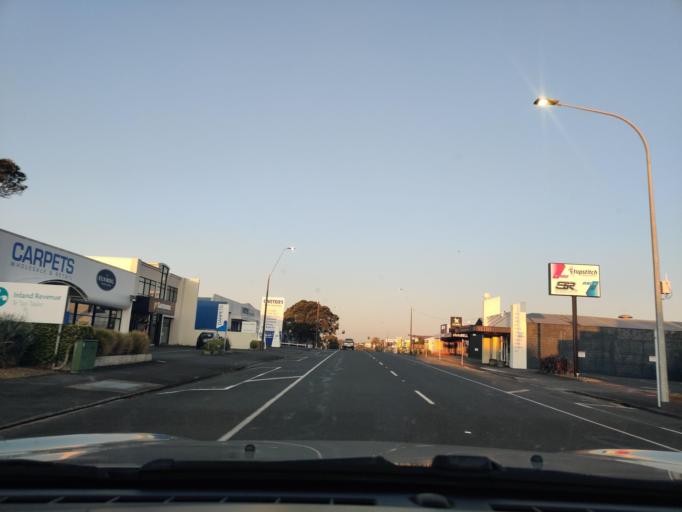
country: NZ
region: Taranaki
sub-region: New Plymouth District
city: New Plymouth
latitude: -39.0546
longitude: 174.0846
